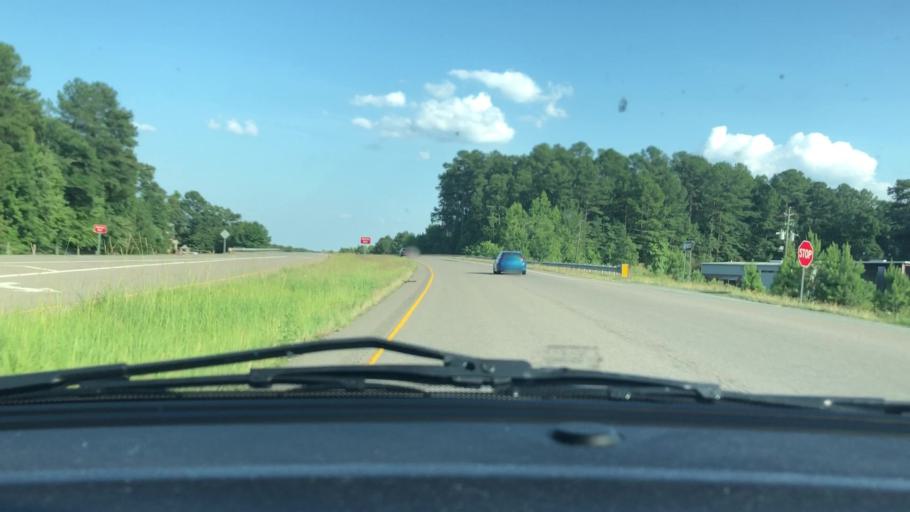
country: US
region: North Carolina
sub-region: Chatham County
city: Farmville
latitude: 35.5605
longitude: -79.2946
